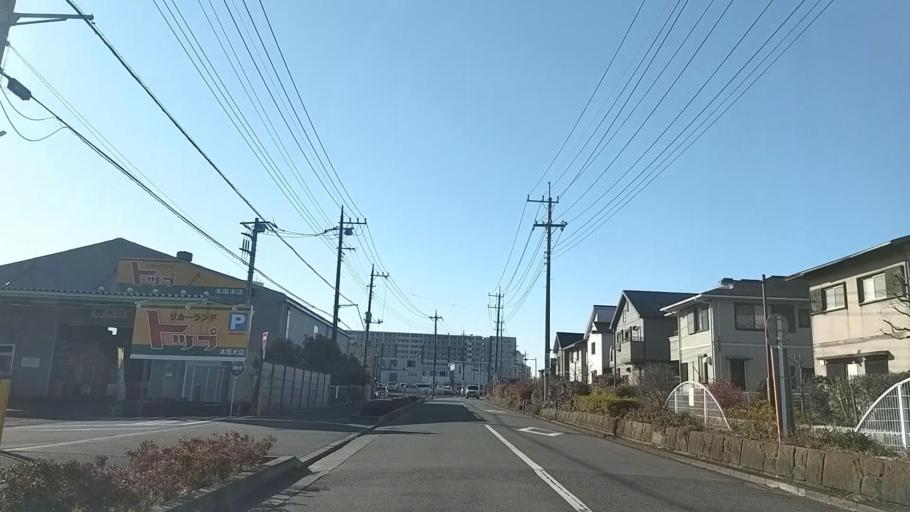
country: JP
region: Kanagawa
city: Atsugi
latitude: 35.4308
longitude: 139.3595
